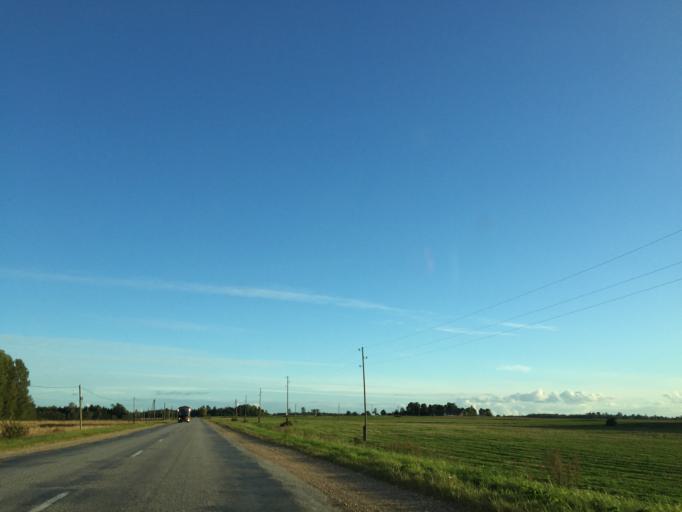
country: LV
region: Saldus Rajons
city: Saldus
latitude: 56.7418
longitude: 22.3775
